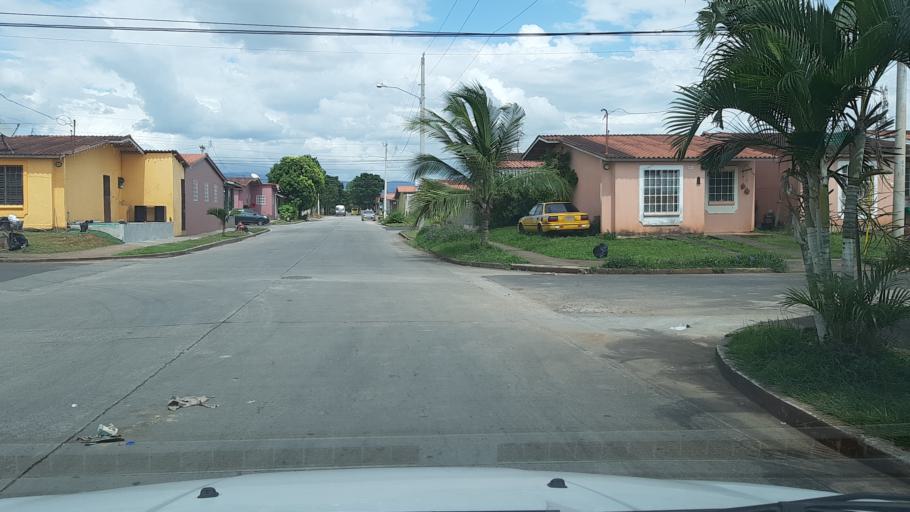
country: PA
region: Panama
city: Tocumen
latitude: 9.0708
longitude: -79.3617
